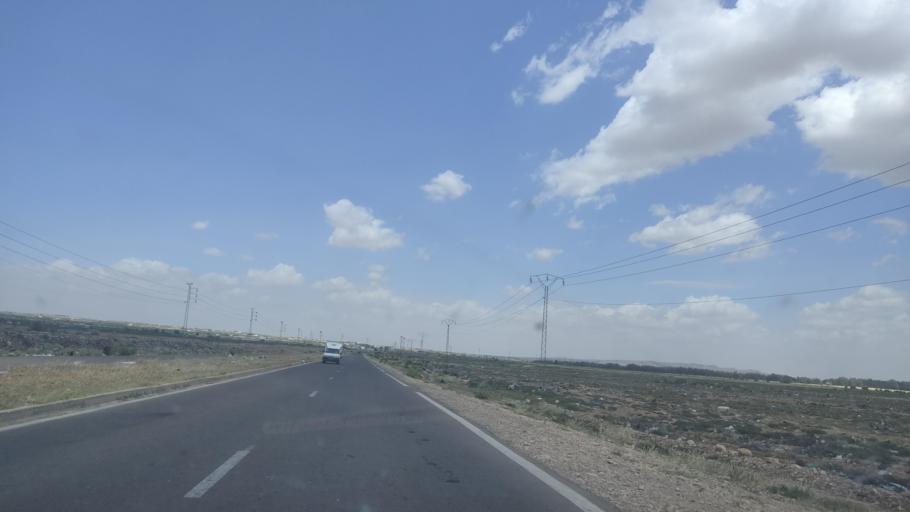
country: TN
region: Al Qasrayn
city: Kasserine
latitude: 35.1977
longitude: 8.8540
